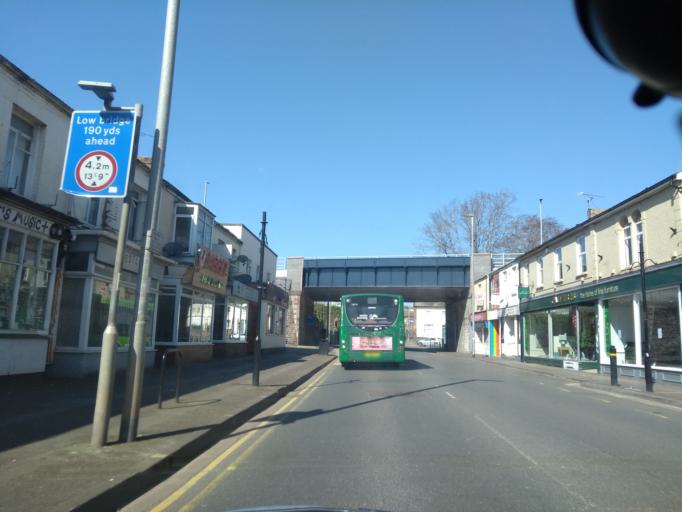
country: GB
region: England
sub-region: Somerset
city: Taunton
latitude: 51.0216
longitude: -3.1033
